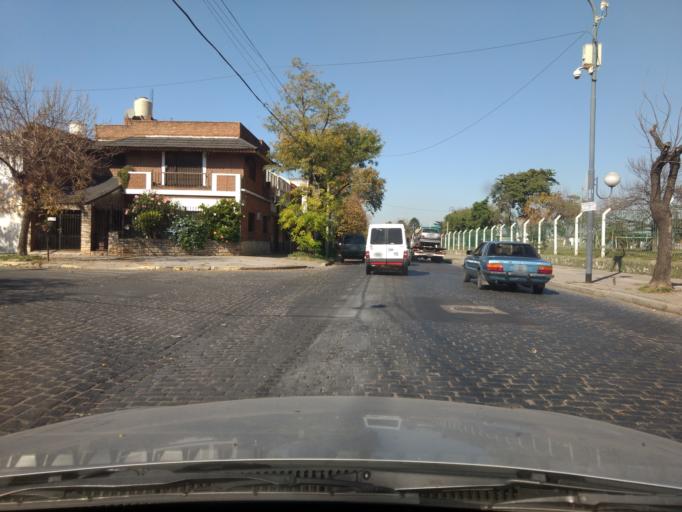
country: AR
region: Buenos Aires F.D.
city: Villa Lugano
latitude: -34.6452
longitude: -58.4750
